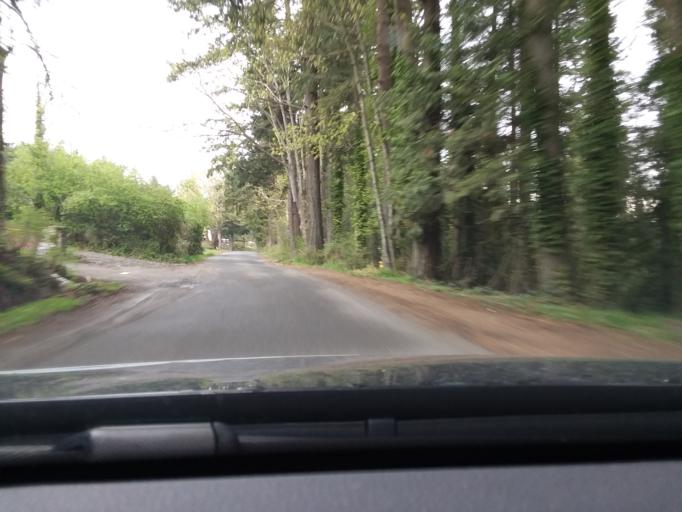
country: CA
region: British Columbia
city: Victoria
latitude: 48.5480
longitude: -123.3899
